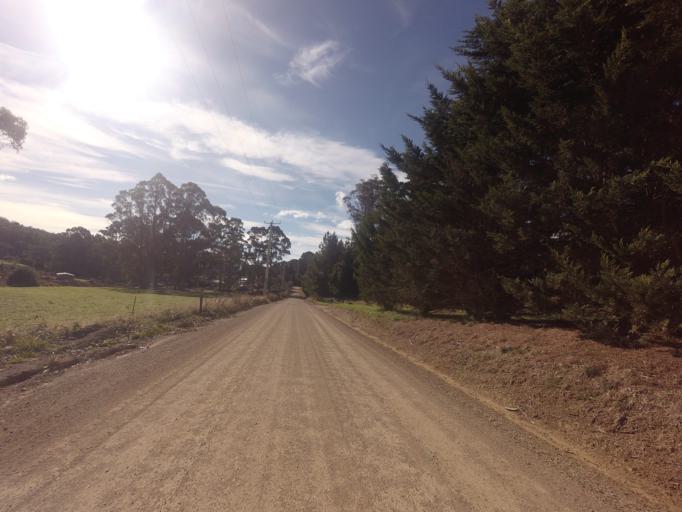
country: AU
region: Tasmania
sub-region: Clarence
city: Sandford
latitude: -43.1491
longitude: 147.7640
